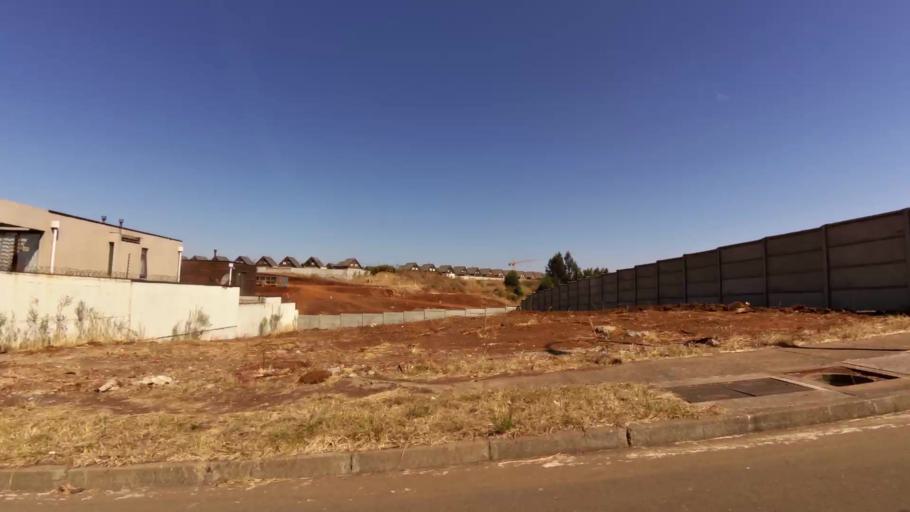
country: CL
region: Biobio
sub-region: Provincia de Concepcion
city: Concepcion
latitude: -36.7841
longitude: -73.0484
